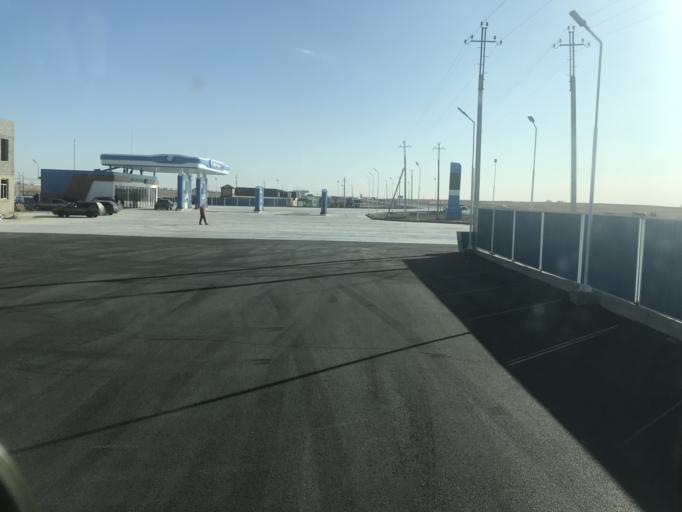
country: KZ
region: Ongtustik Qazaqstan
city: Temirlanovka
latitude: 42.5713
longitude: 69.3109
